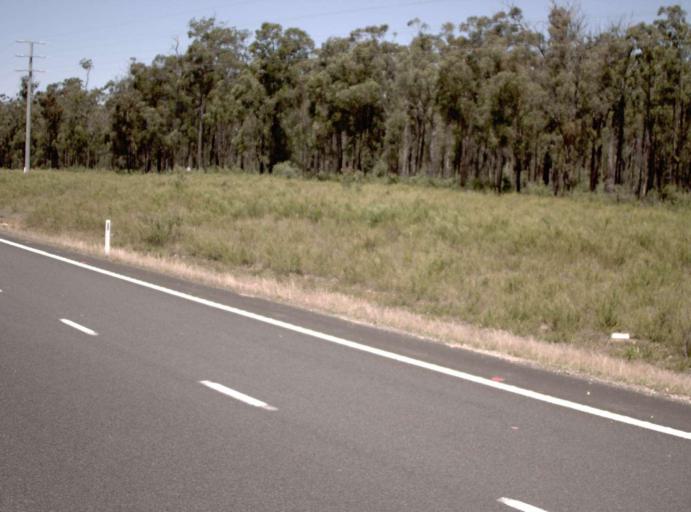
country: AU
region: Victoria
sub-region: East Gippsland
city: Lakes Entrance
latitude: -37.7336
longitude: 148.1442
